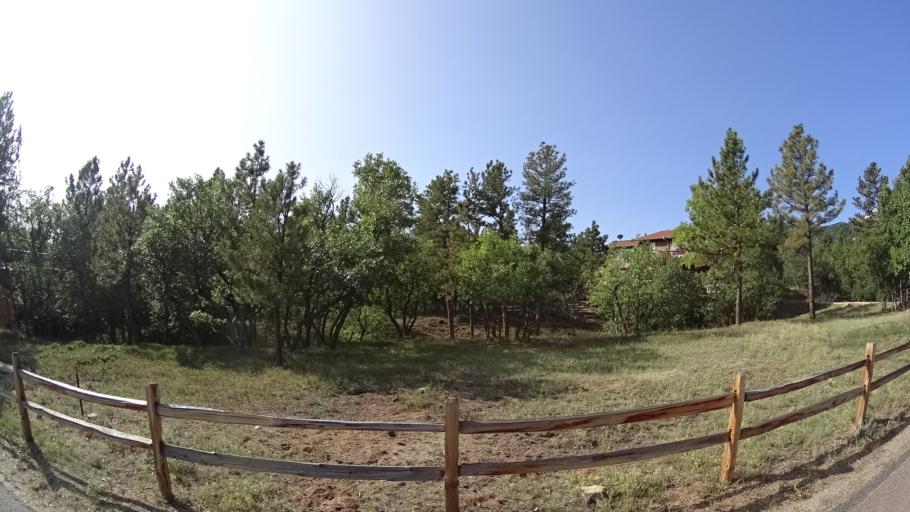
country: US
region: Colorado
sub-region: El Paso County
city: Colorado Springs
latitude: 38.8110
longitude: -104.8660
